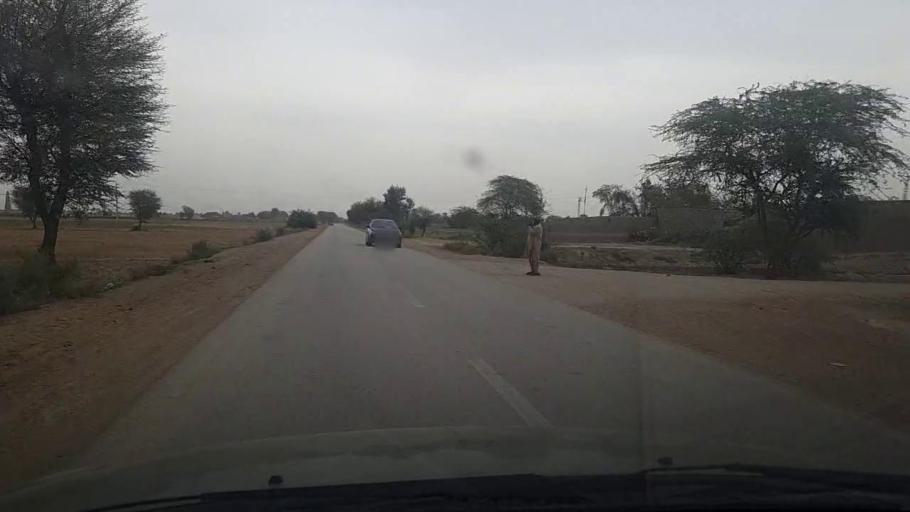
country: PK
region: Sindh
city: Daulatpur
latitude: 26.3328
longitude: 68.1156
